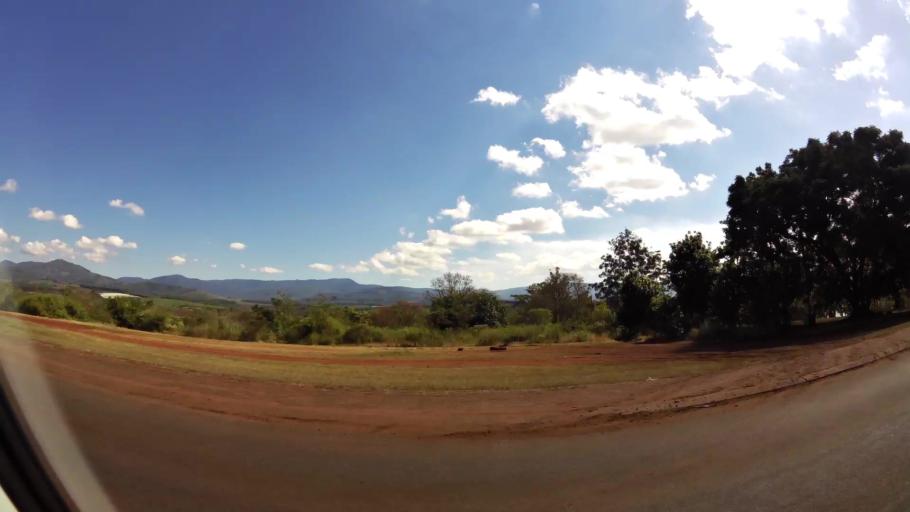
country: ZA
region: Limpopo
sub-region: Mopani District Municipality
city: Tzaneen
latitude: -23.8150
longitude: 30.1469
